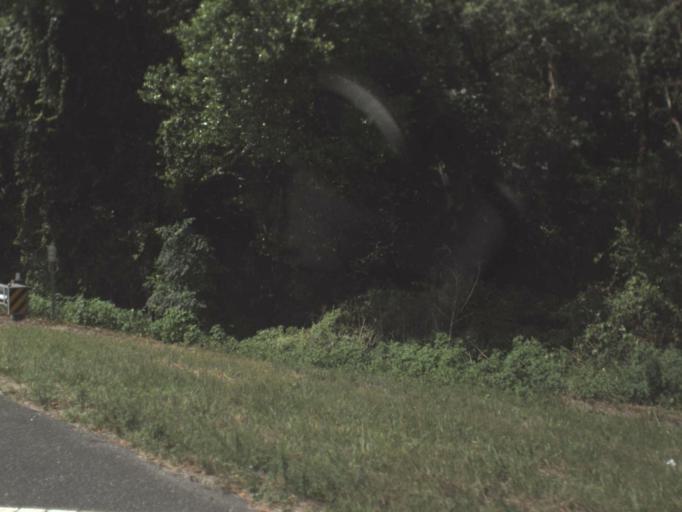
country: US
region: Florida
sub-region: Baker County
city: Macclenny
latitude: 30.3536
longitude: -82.1296
